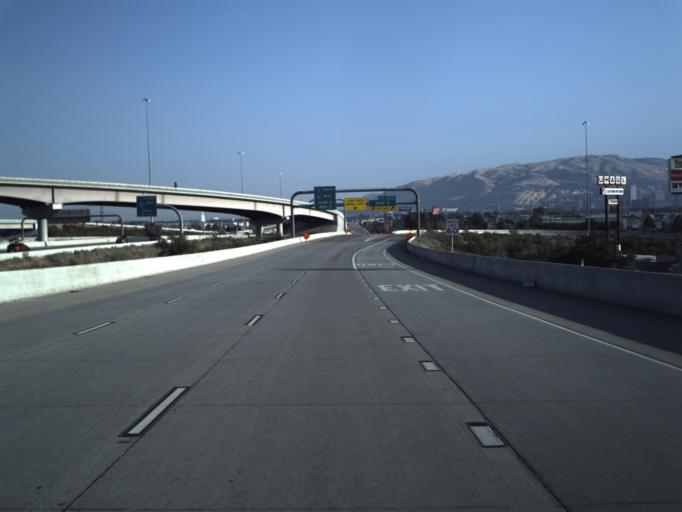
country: US
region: Utah
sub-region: Salt Lake County
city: South Salt Lake
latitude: 40.7233
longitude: -111.9035
